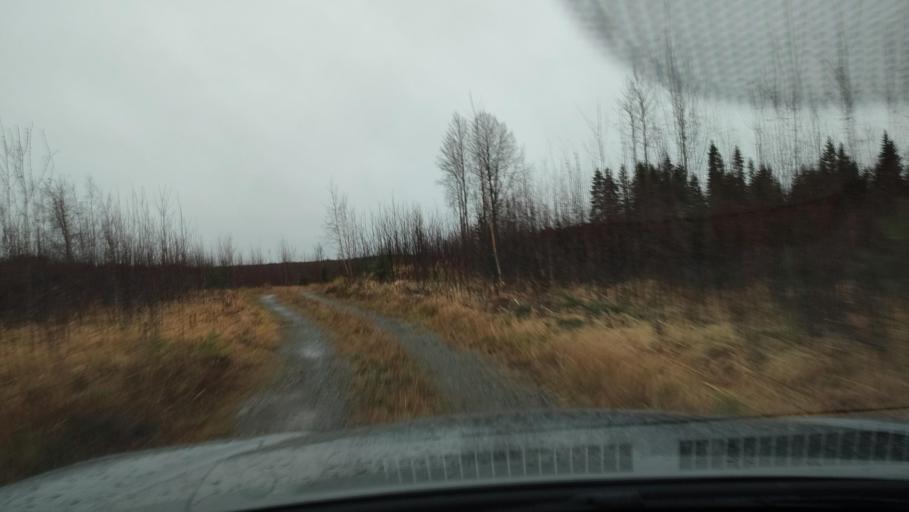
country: FI
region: Southern Ostrobothnia
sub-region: Suupohja
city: Karijoki
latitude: 62.2255
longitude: 21.5515
